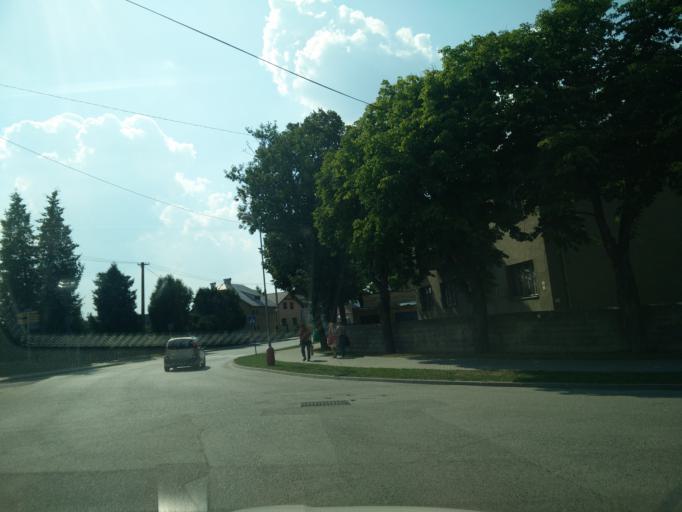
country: SK
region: Zilinsky
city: Rajec
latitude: 49.0885
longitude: 18.6429
